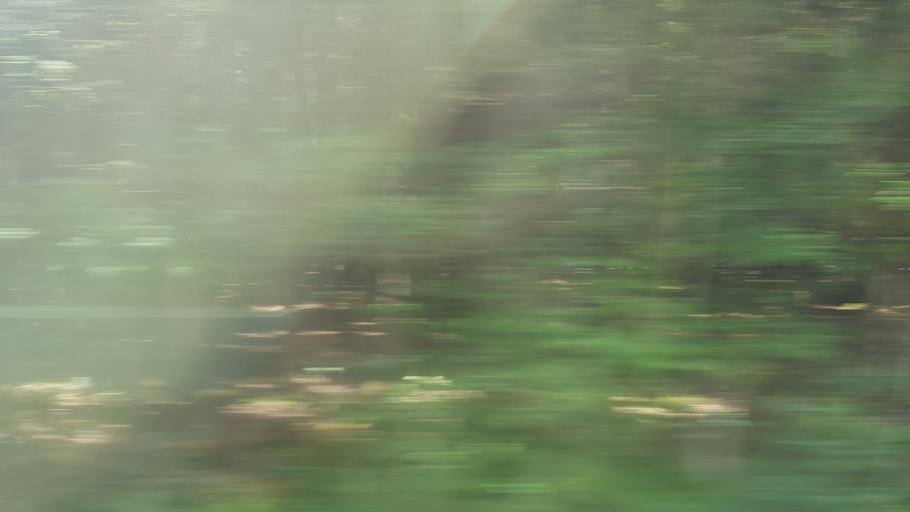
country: SE
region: Vaestra Goetaland
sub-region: Kungalvs Kommun
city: Kode
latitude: 57.9689
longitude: 11.8363
